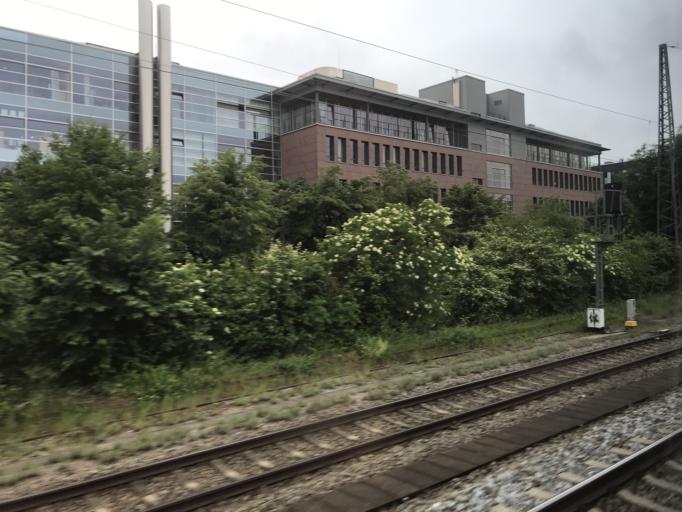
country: DE
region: Bavaria
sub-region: Upper Bavaria
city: Pasing
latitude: 48.1441
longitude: 11.5022
